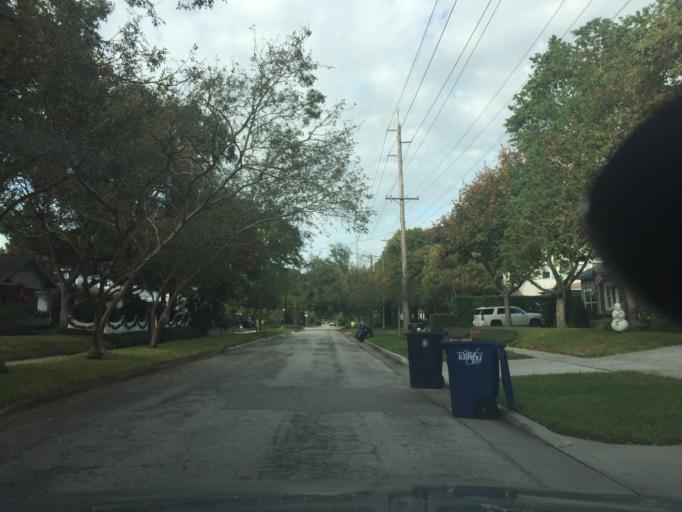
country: US
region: Florida
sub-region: Hillsborough County
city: Tampa
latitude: 27.9418
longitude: -82.4954
